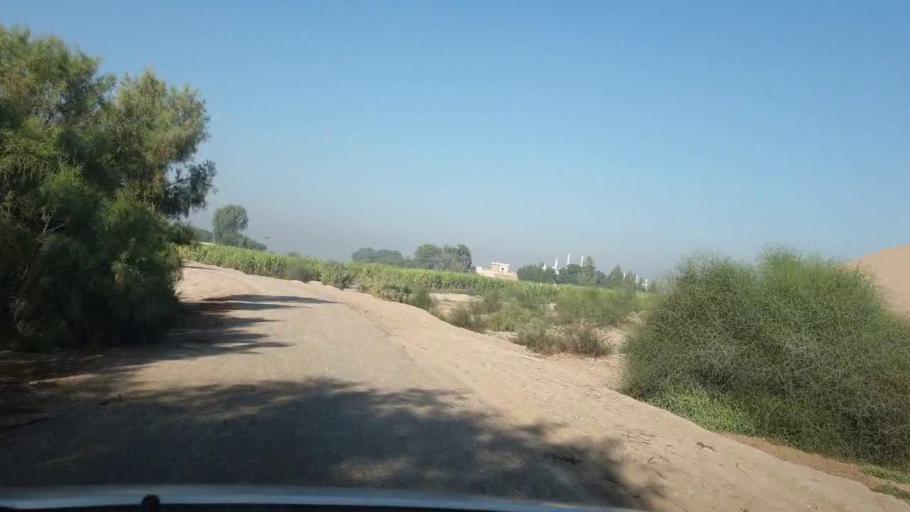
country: PK
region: Sindh
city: Dadu
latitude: 26.6761
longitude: 67.8341
